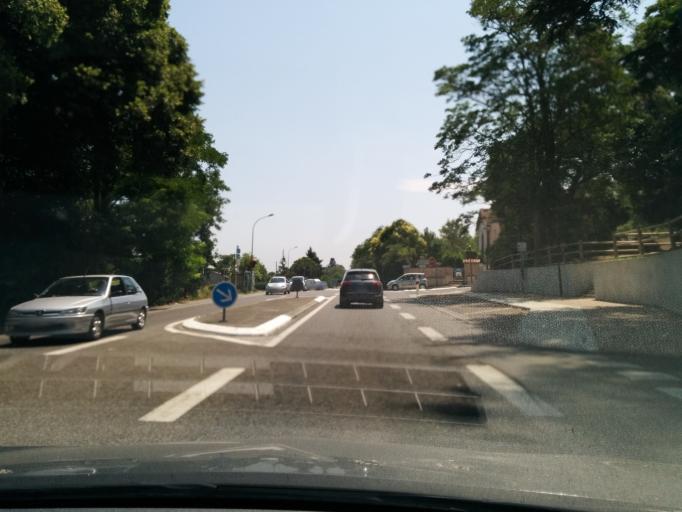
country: FR
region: Midi-Pyrenees
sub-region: Departement de la Haute-Garonne
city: Pechabou
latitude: 43.5039
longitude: 1.5100
